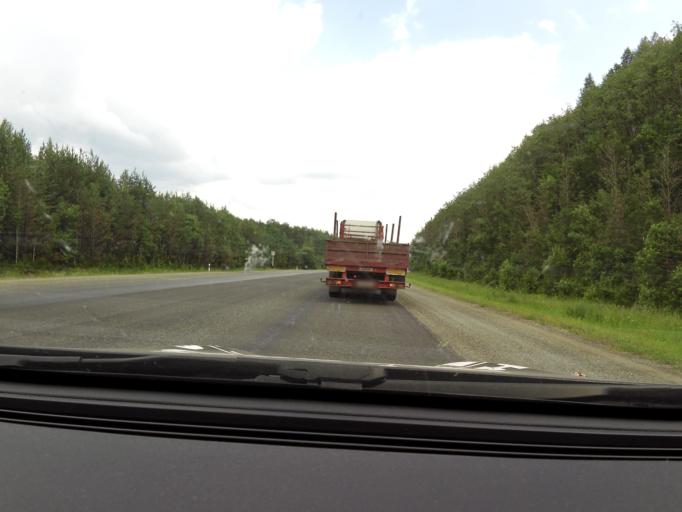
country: RU
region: Sverdlovsk
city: Ufimskiy
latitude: 56.7857
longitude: 58.3128
